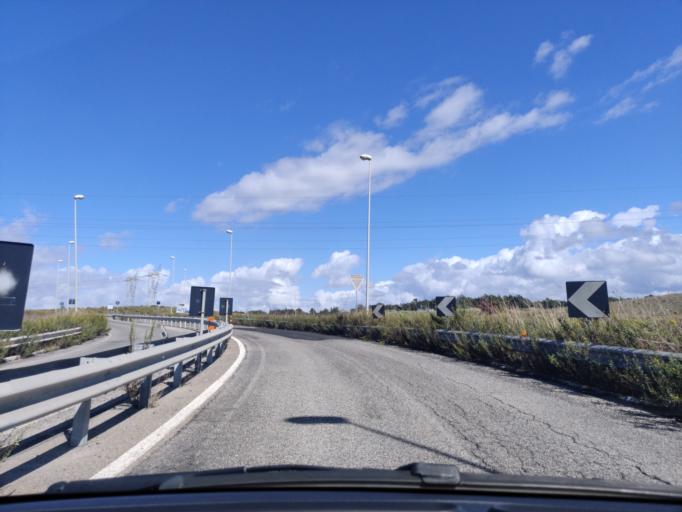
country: IT
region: Latium
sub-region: Citta metropolitana di Roma Capitale
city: Aurelia
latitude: 42.1282
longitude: 11.7941
